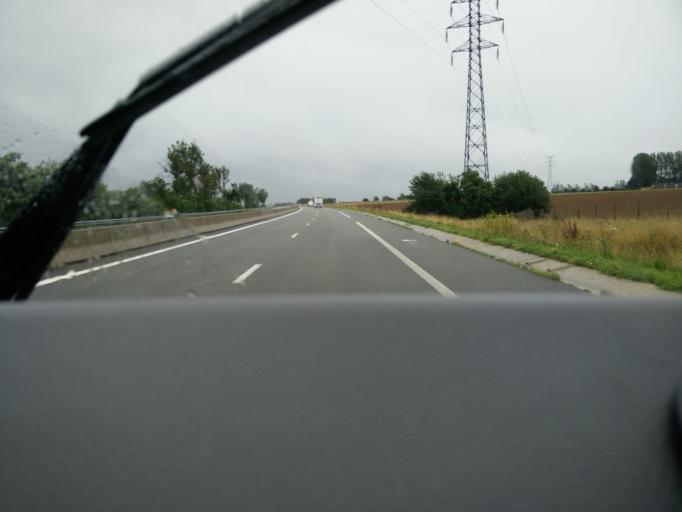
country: FR
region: Nord-Pas-de-Calais
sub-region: Departement du Pas-de-Calais
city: Marconnelle
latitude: 50.3610
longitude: 1.9827
